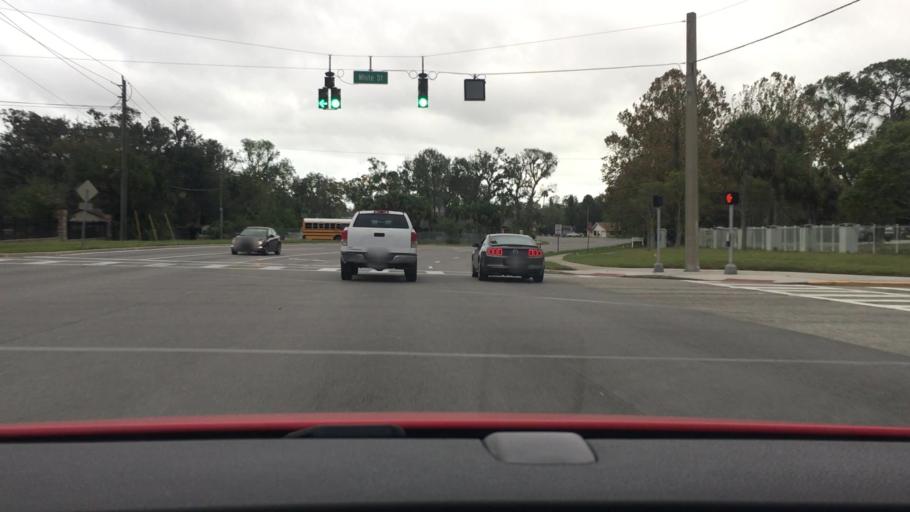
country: US
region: Florida
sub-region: Volusia County
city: Daytona Beach
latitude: 29.2092
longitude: -81.0501
